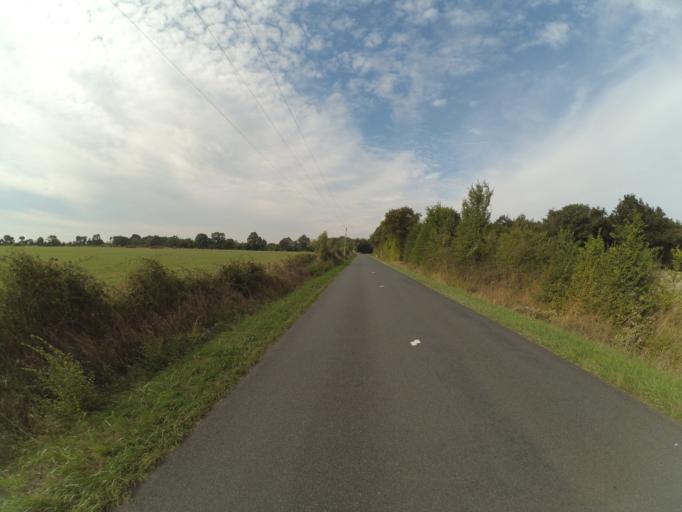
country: FR
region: Pays de la Loire
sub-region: Departement de Maine-et-Loire
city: Saint-Jean
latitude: 47.1918
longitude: -0.3474
